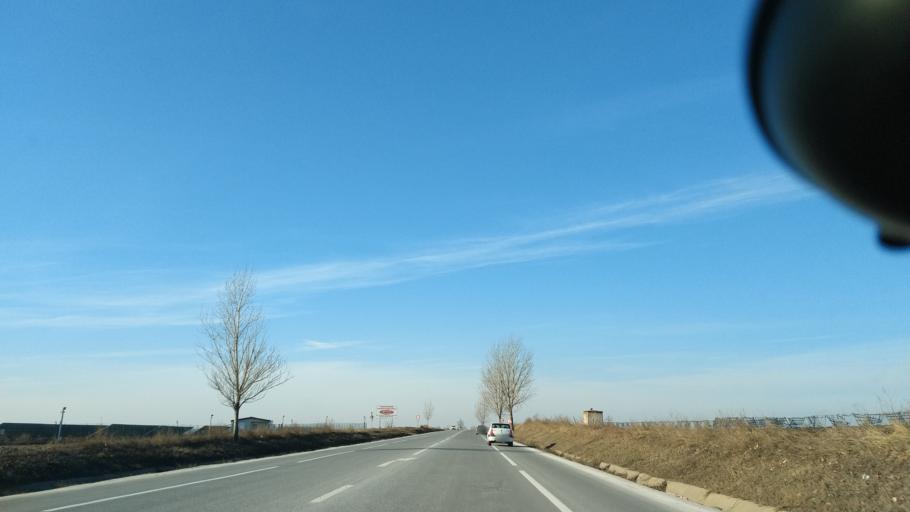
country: RO
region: Iasi
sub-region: Comuna Podu Iloaiei
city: Budai
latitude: 47.2225
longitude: 27.1969
